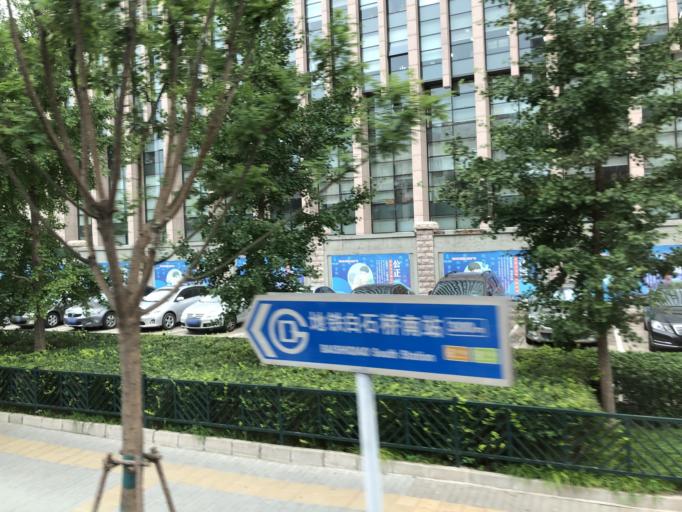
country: CN
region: Beijing
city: Jinrongjie
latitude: 39.9352
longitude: 116.3193
